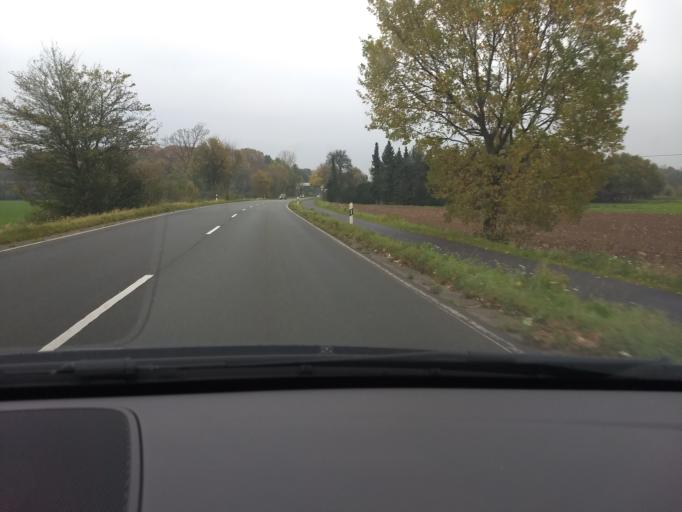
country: DE
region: North Rhine-Westphalia
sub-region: Regierungsbezirk Munster
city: Borken
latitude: 51.8273
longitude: 6.8531
